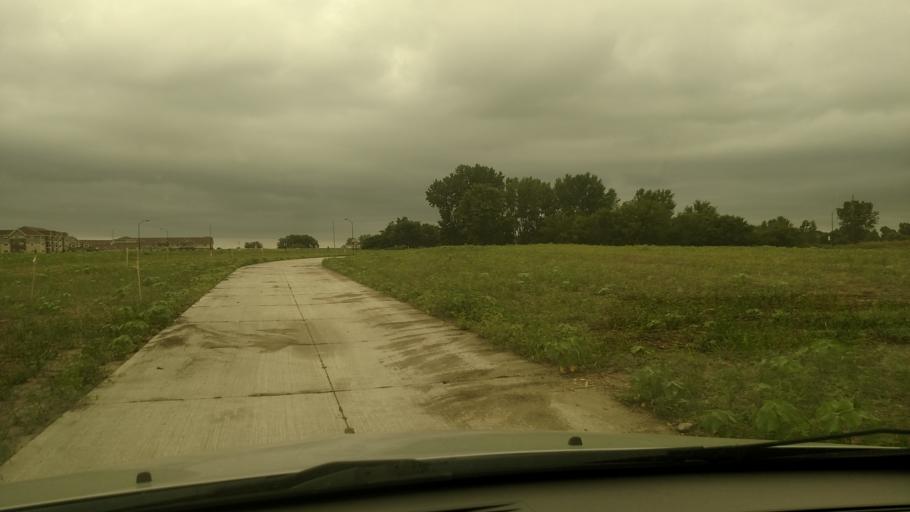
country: US
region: Iowa
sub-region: Polk County
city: Ankeny
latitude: 41.7151
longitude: -93.6123
